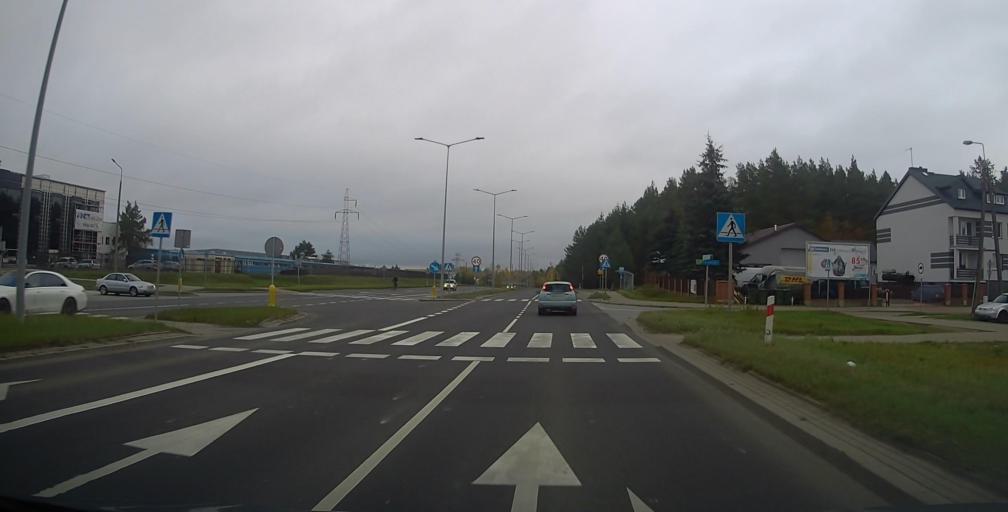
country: PL
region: Warmian-Masurian Voivodeship
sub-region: Powiat elcki
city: Elk
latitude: 53.8143
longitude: 22.3833
